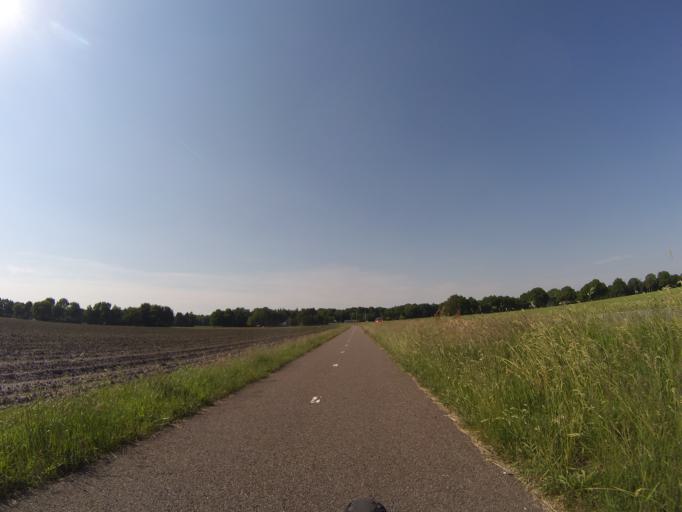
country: NL
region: Drenthe
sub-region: Gemeente Coevorden
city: Sleen
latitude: 52.7602
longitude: 6.8169
